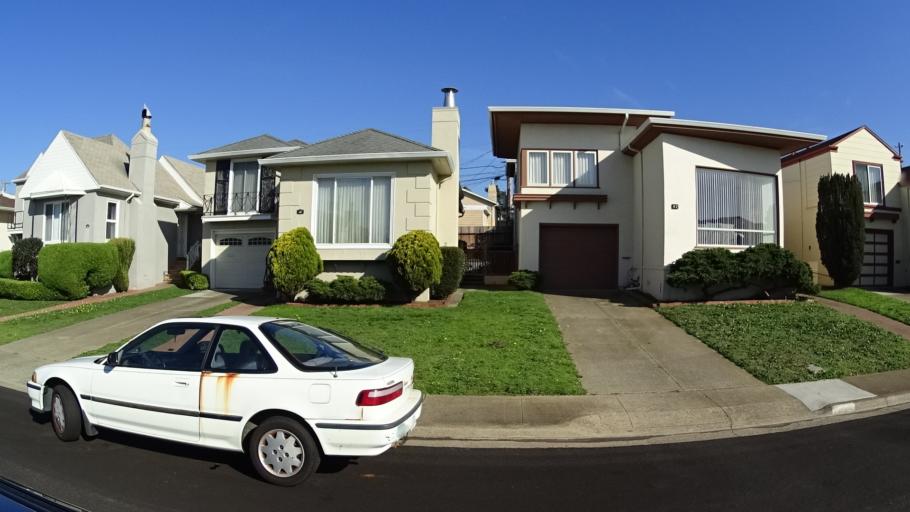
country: US
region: California
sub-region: San Mateo County
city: Broadmoor
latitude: 37.7045
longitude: -122.4808
